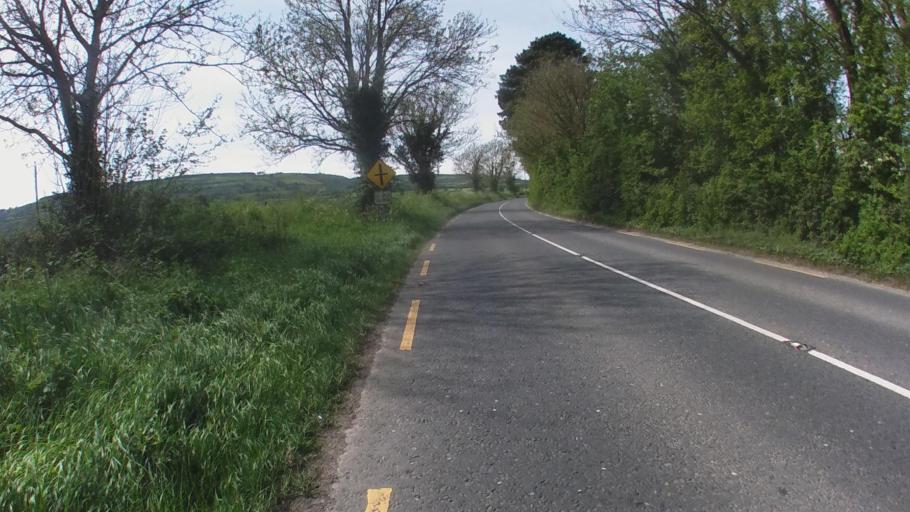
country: IE
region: Leinster
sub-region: County Carlow
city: Carlow
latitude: 52.8419
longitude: -6.9747
